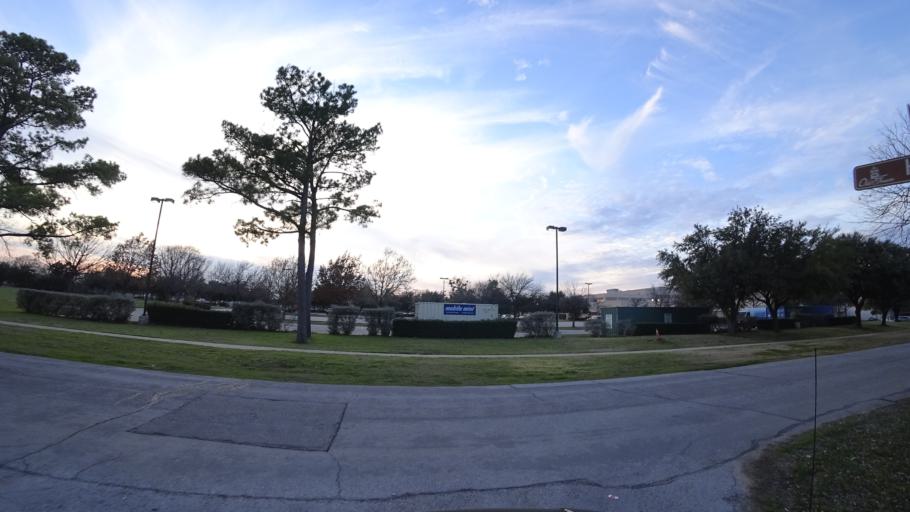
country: US
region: Texas
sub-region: Denton County
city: Lewisville
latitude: 33.0437
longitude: -97.0031
